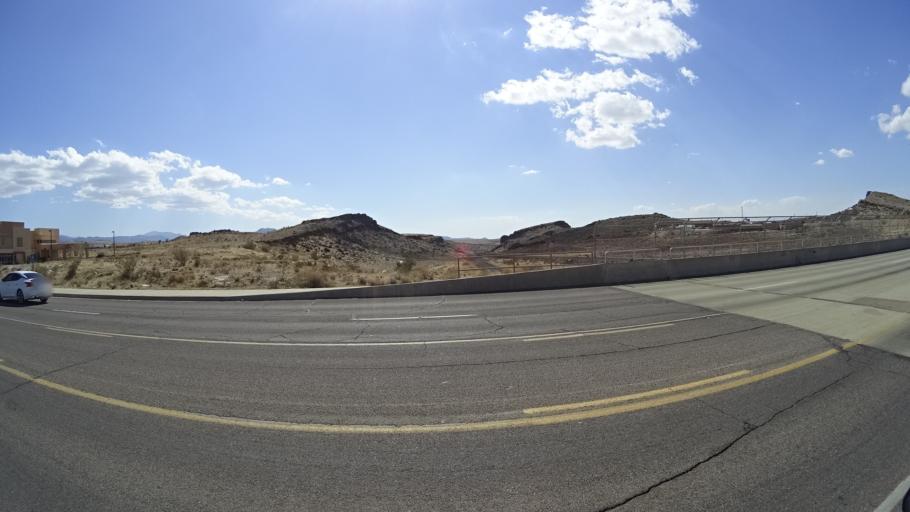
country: US
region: Arizona
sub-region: Mohave County
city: Kingman
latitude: 35.1937
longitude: -114.0282
